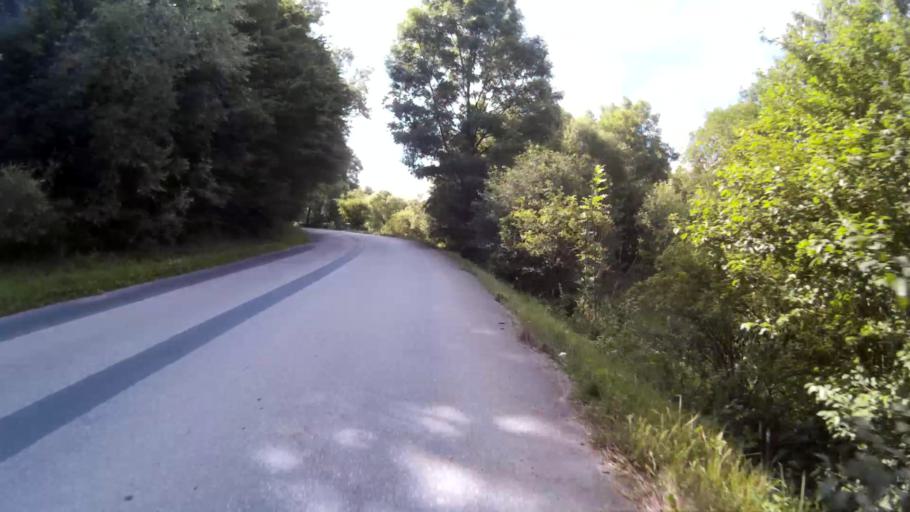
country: CZ
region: South Moravian
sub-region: Okres Brno-Venkov
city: Rosice
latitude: 49.1696
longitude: 16.4179
